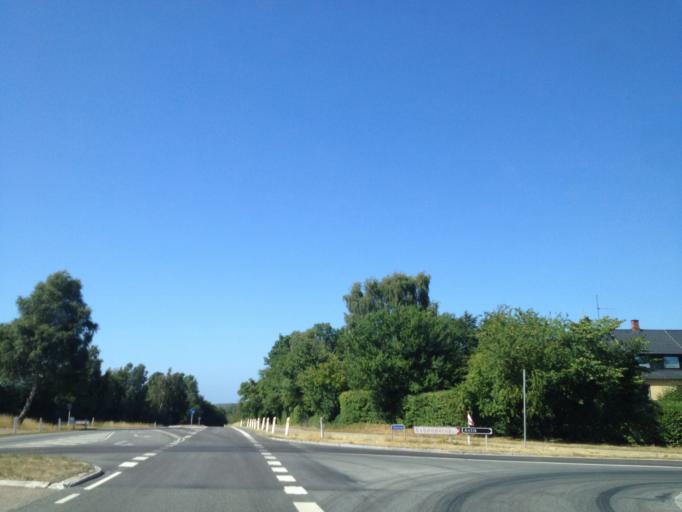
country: DK
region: Capital Region
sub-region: Gribskov Kommune
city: Graested
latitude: 56.0515
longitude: 12.3413
